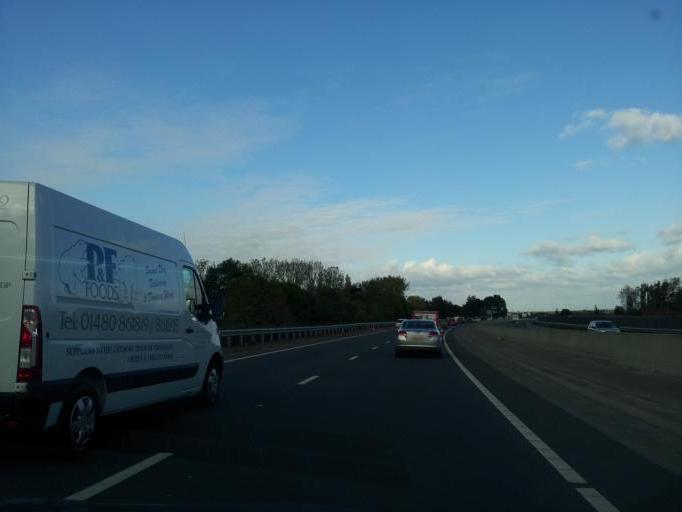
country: GB
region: England
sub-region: Central Bedfordshire
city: Lidlington
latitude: 52.0459
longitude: -0.5873
